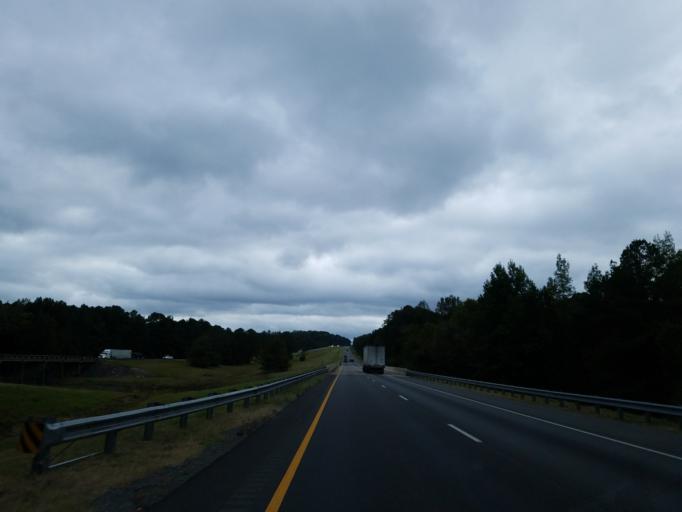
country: US
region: Alabama
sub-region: Hale County
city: Moundville
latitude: 33.0000
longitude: -87.7712
